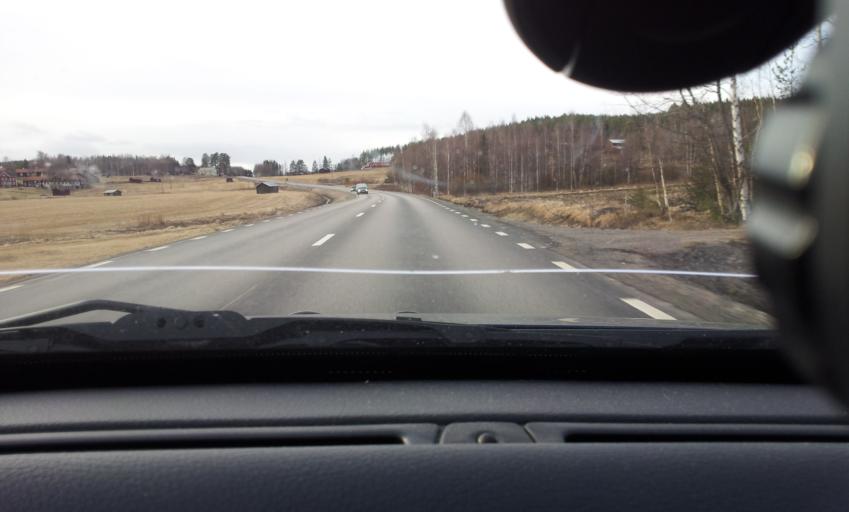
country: SE
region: Gaevleborg
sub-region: Ljusdals Kommun
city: Farila
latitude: 61.8605
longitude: 15.7420
